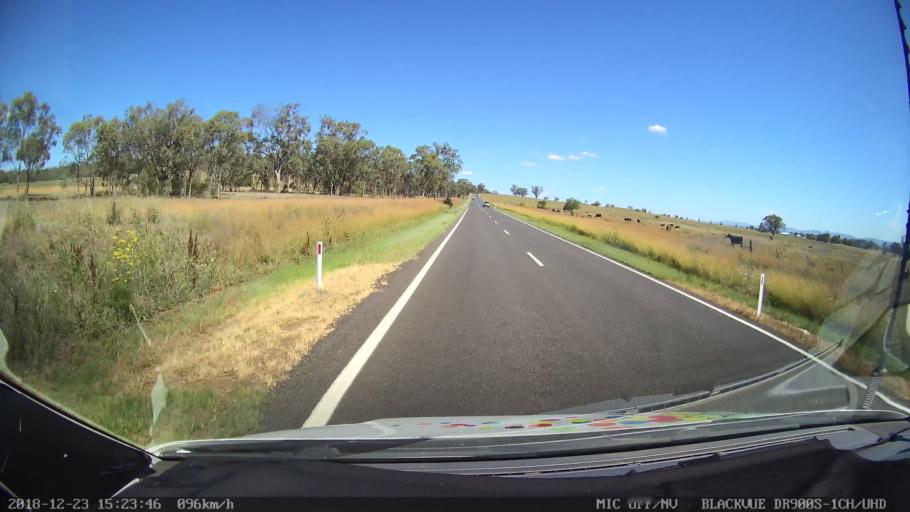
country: AU
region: New South Wales
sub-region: Tamworth Municipality
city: Manilla
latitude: -30.8840
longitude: 150.8172
